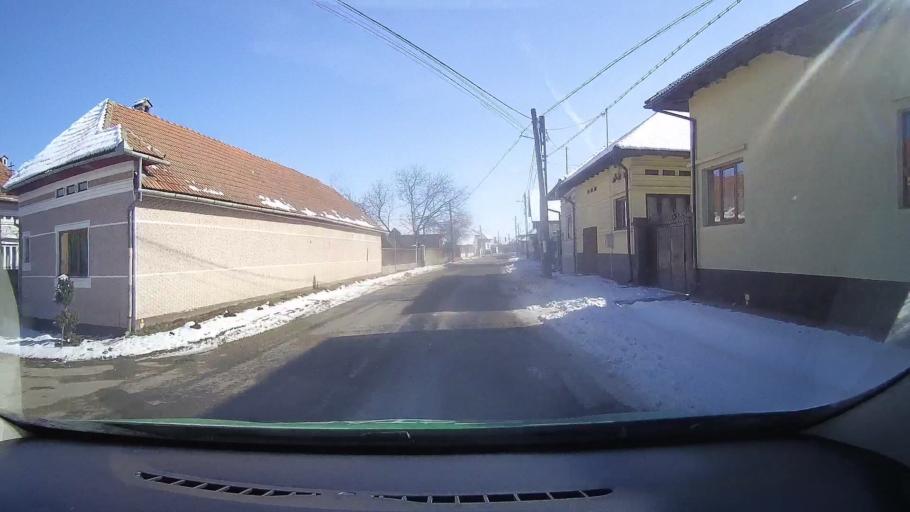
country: RO
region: Brasov
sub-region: Comuna Recea
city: Recea
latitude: 45.7318
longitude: 24.9444
